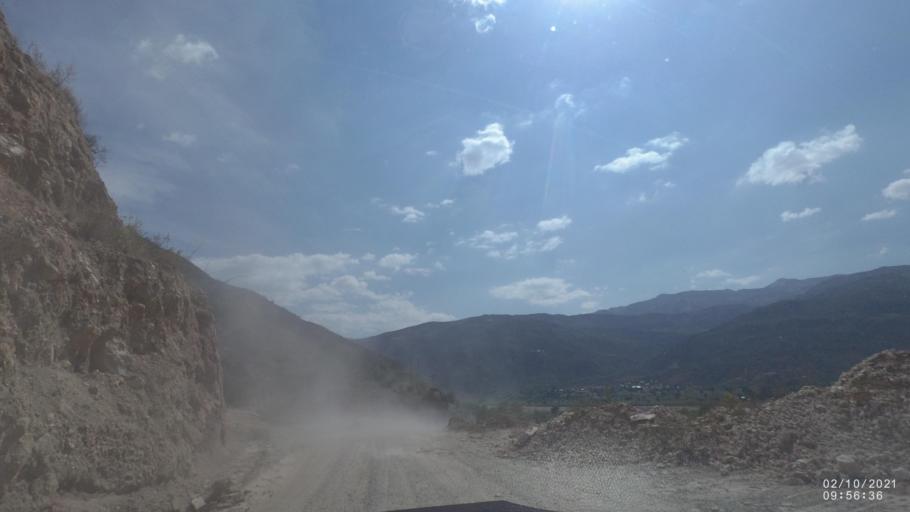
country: BO
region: Cochabamba
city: Irpa Irpa
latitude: -17.7918
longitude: -66.3456
